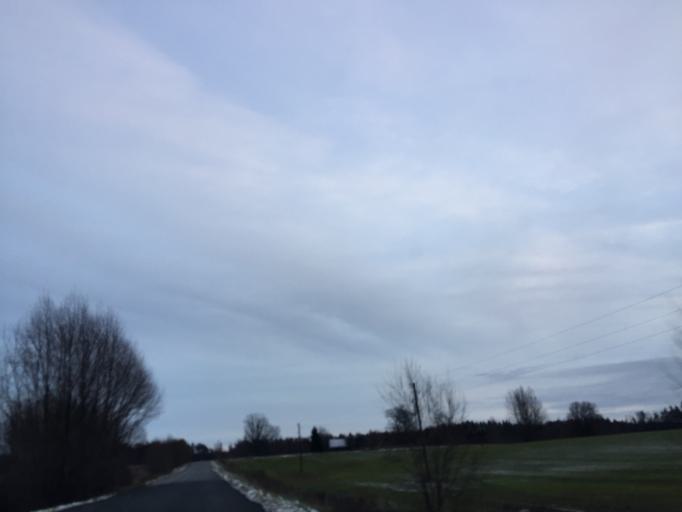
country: LV
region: Burtnieki
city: Matisi
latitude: 57.6470
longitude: 25.0151
